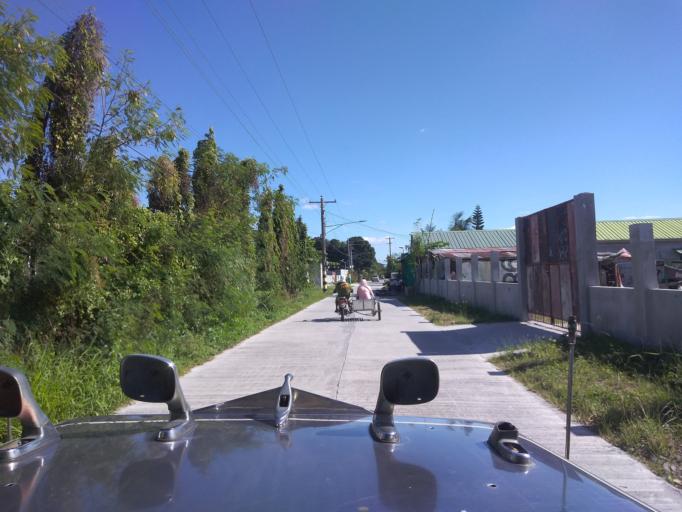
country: PH
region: Central Luzon
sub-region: Province of Pampanga
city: Bacolor
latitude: 15.0236
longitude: 120.6375
